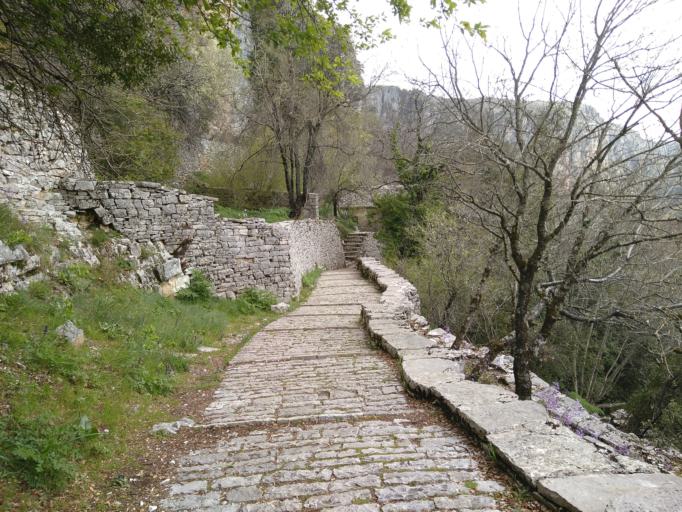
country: GR
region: Epirus
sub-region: Nomos Ioanninon
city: Asprangeloi
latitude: 39.8865
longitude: 20.7536
